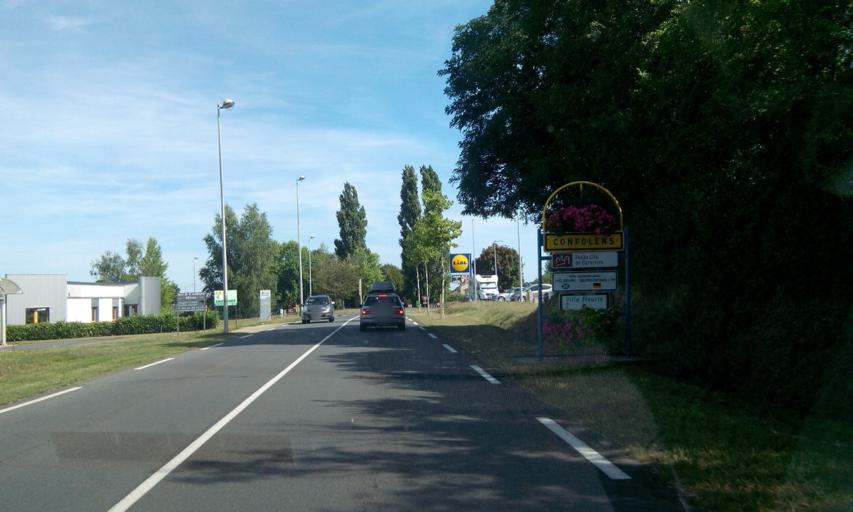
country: FR
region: Poitou-Charentes
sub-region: Departement de la Charente
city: Confolens
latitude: 46.0023
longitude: 0.6739
